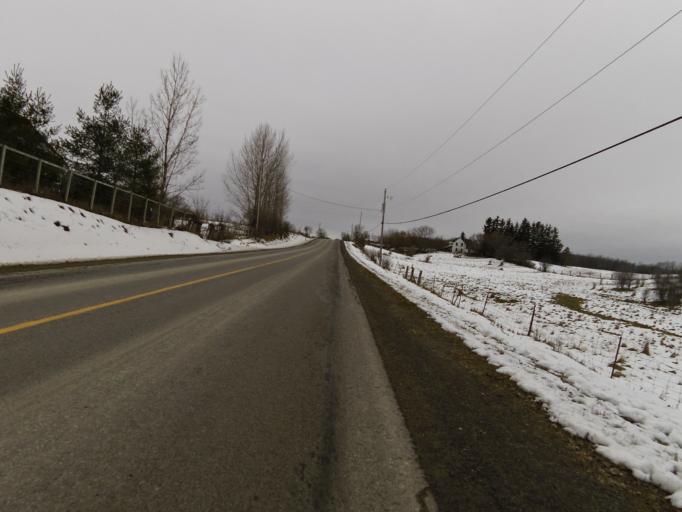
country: CA
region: Ontario
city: Carleton Place
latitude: 45.2149
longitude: -76.2016
